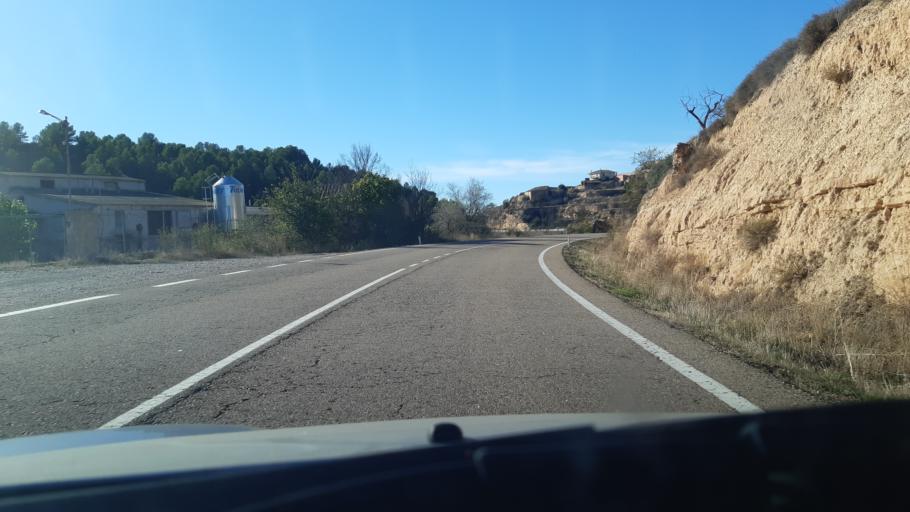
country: ES
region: Aragon
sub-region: Provincia de Teruel
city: Valjunquera
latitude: 40.9495
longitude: 0.0320
